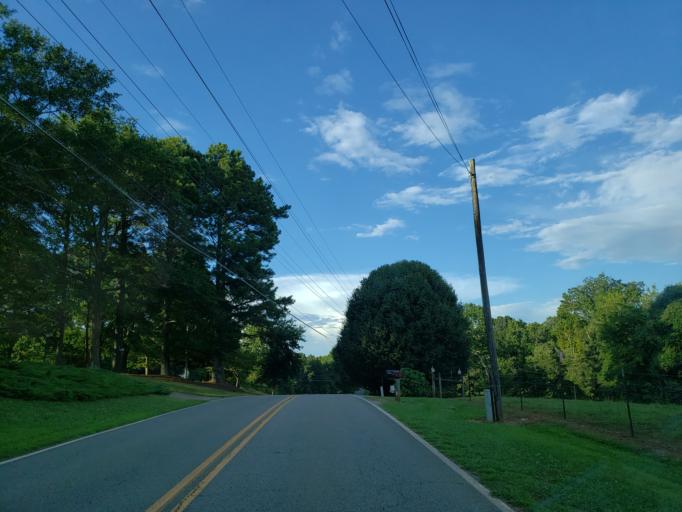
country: US
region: Georgia
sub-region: Cherokee County
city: Canton
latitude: 34.3157
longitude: -84.5306
